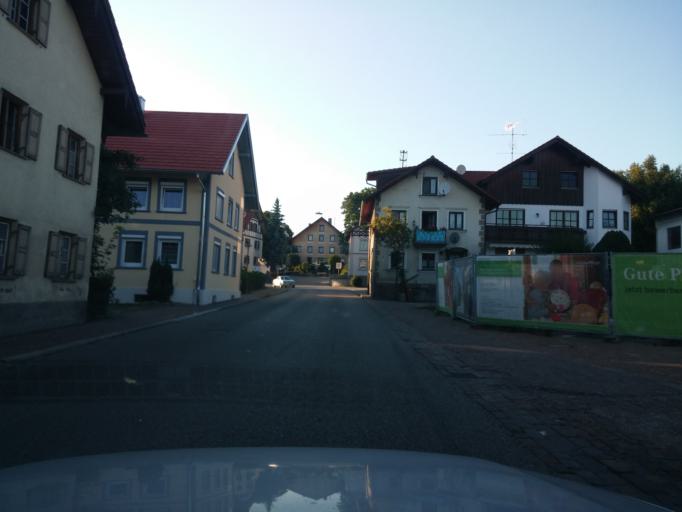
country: DE
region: Bavaria
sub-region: Swabia
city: Altusried
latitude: 47.8056
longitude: 10.2141
